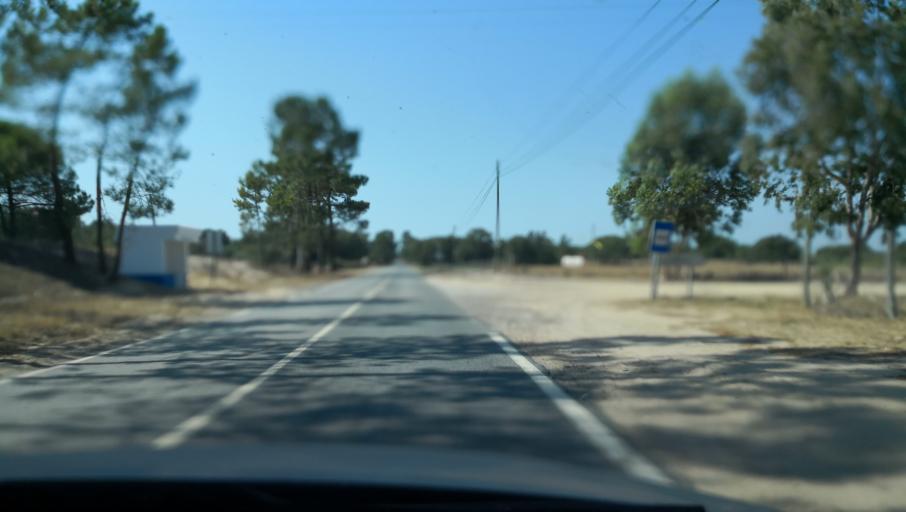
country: PT
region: Setubal
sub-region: Alcacer do Sal
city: Alcacer do Sal
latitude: 38.4048
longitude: -8.6816
